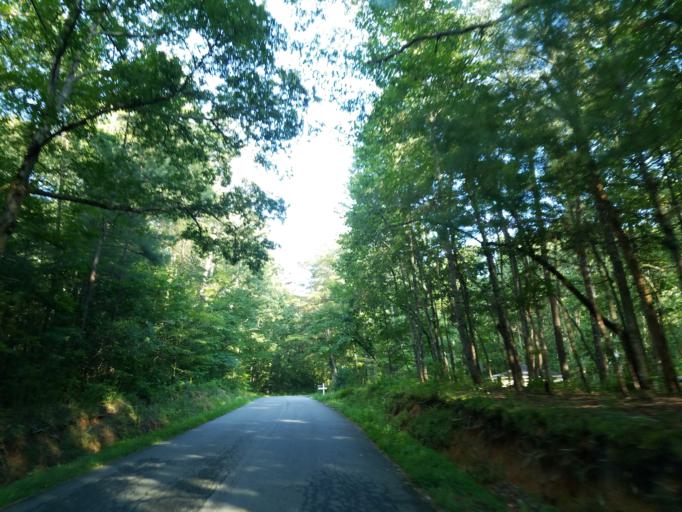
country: US
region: Georgia
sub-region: Gilmer County
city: Ellijay
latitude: 34.6413
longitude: -84.3329
